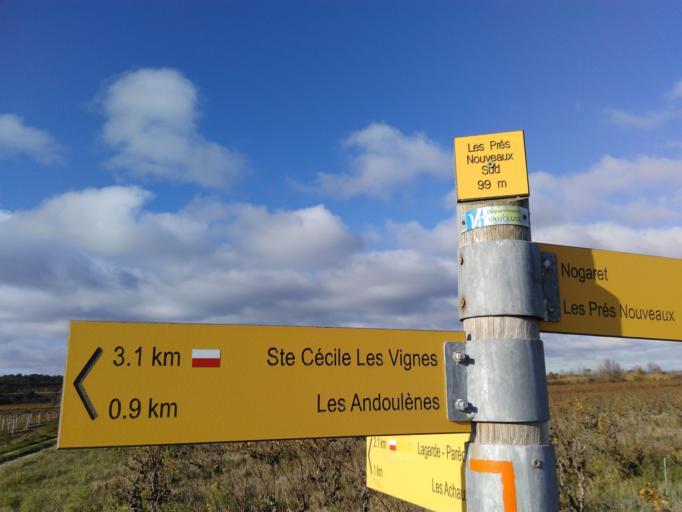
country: FR
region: Provence-Alpes-Cote d'Azur
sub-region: Departement du Vaucluse
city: Sainte-Cecile-les-Vignes
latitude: 44.2341
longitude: 4.8691
